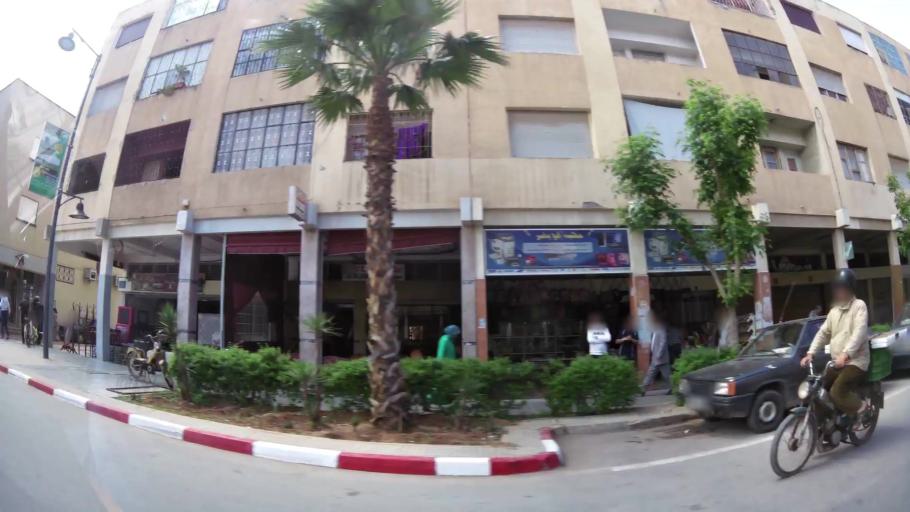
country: MA
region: Oriental
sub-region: Oujda-Angad
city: Oujda
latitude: 34.6797
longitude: -1.9025
